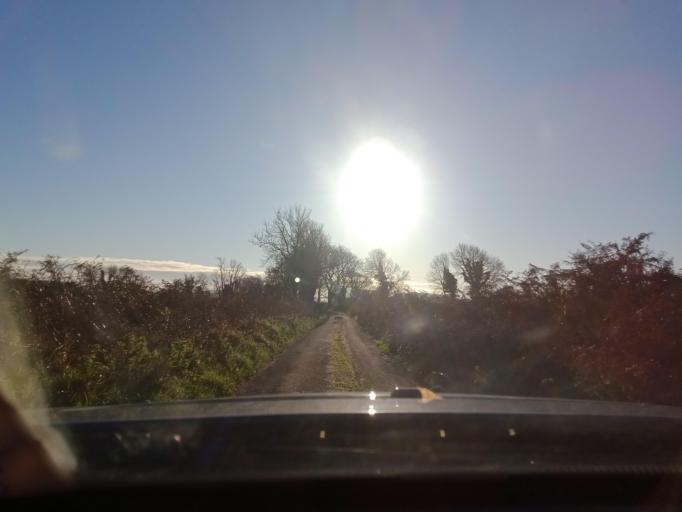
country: IE
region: Leinster
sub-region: Kilkenny
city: Callan
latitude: 52.4511
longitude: -7.4193
